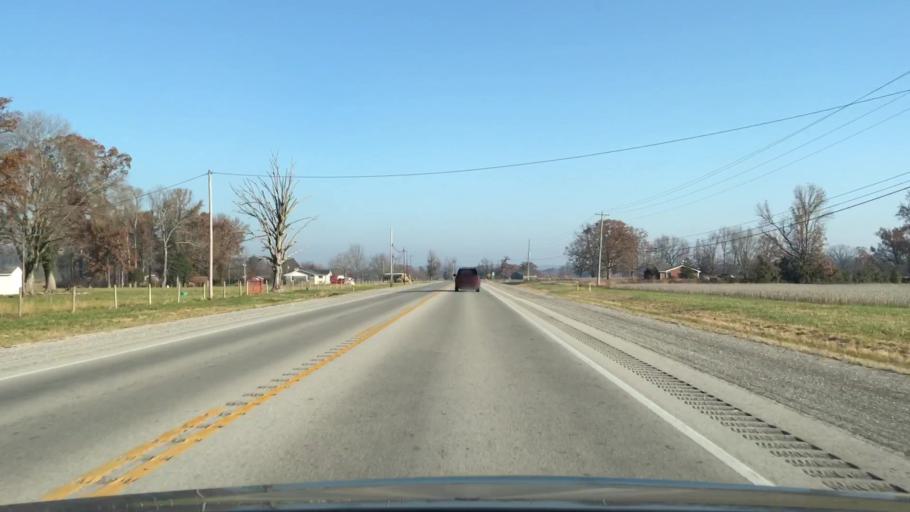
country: US
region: Kentucky
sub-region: Edmonson County
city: Brownsville
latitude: 37.1376
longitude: -86.2315
